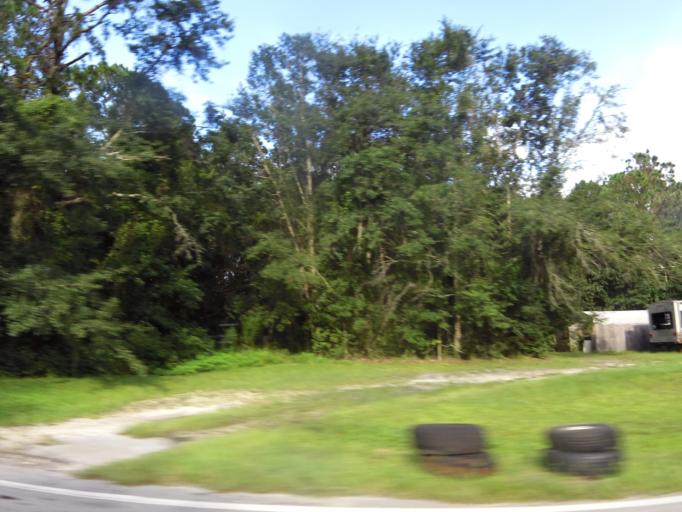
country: US
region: Florida
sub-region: Saint Johns County
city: Fruit Cove
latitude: 30.1471
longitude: -81.5957
